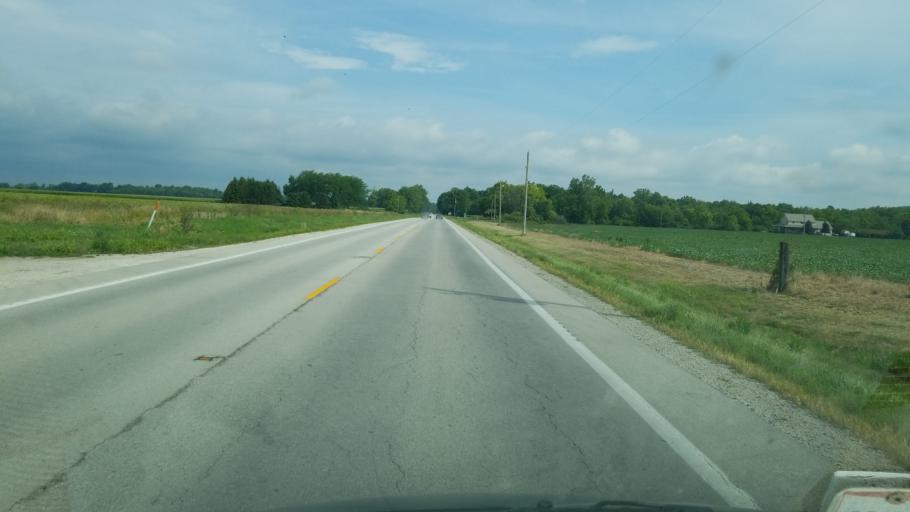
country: US
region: Ohio
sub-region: Sandusky County
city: Ballville
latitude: 41.2599
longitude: -83.1678
